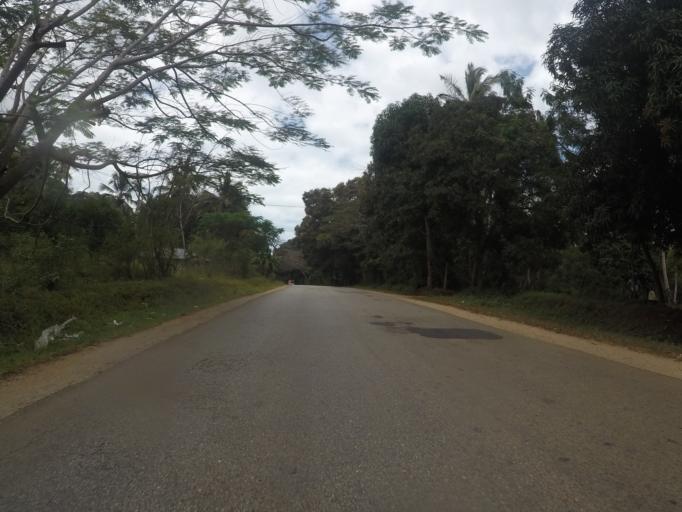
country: TZ
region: Zanzibar Central/South
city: Koani
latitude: -6.2074
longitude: 39.3247
